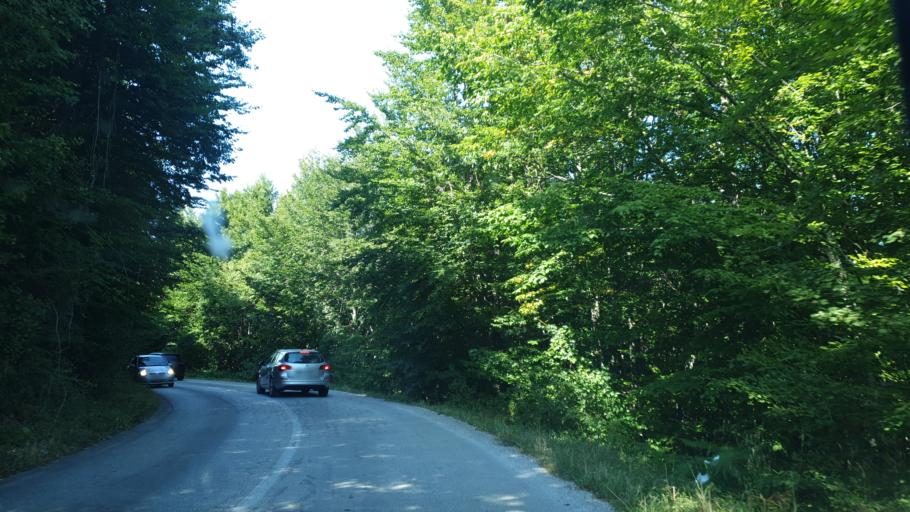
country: RS
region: Central Serbia
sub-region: Zlatiborski Okrug
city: Cajetina
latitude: 43.7056
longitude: 19.8437
